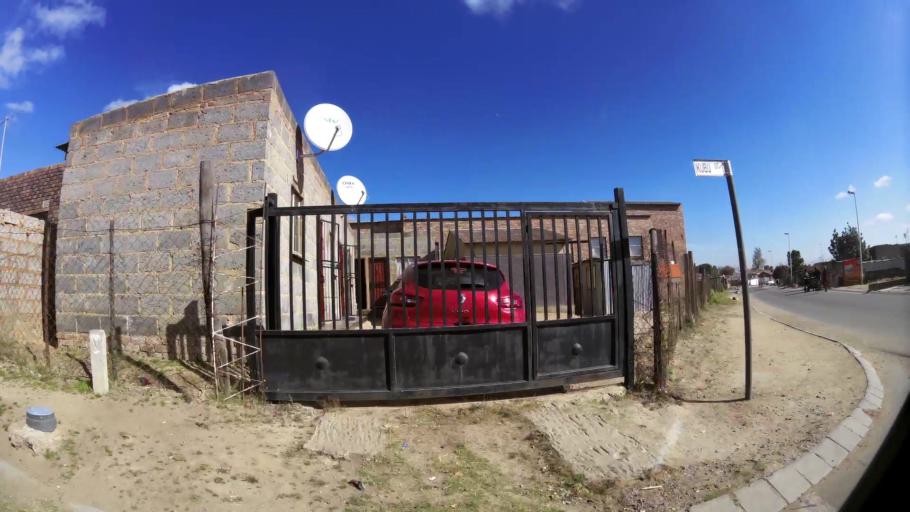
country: ZA
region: Gauteng
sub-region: City of Johannesburg Metropolitan Municipality
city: Modderfontein
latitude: -26.0426
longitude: 28.1787
